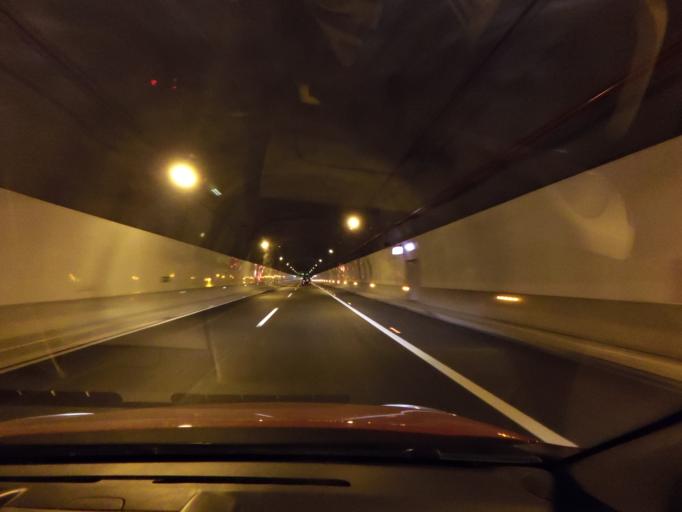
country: ES
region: Canary Islands
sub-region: Provincia de Las Palmas
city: Puerto Rico
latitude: 27.8083
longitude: -15.7203
